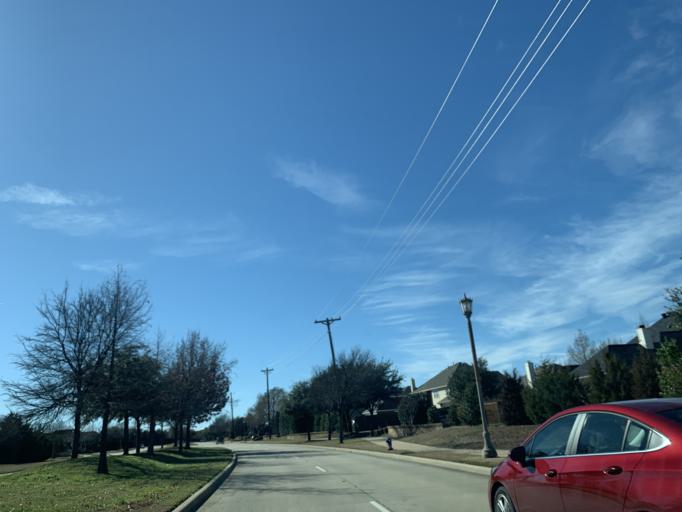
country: US
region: Texas
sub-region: Denton County
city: The Colony
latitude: 33.0864
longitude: -96.8598
